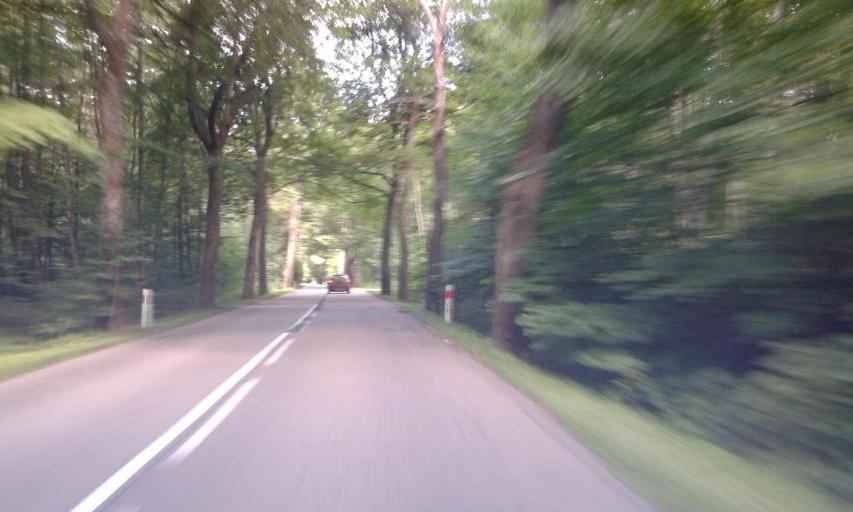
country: PL
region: West Pomeranian Voivodeship
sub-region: Powiat koszalinski
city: Polanow
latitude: 54.2238
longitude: 16.6977
